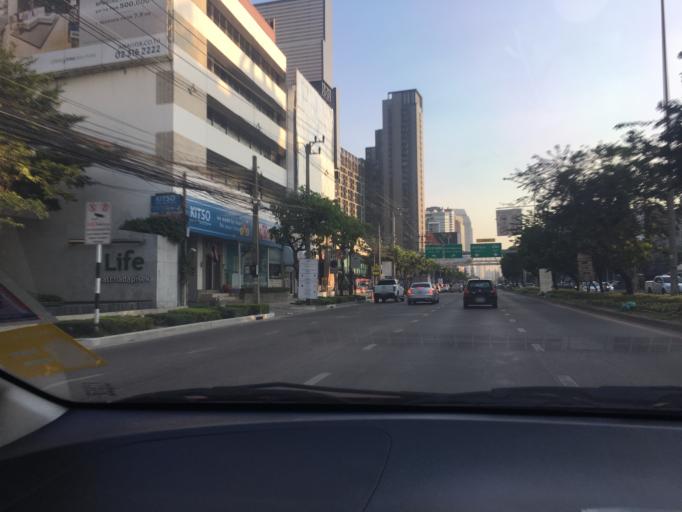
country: TH
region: Bangkok
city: Huai Khwang
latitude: 13.7832
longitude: 100.5739
